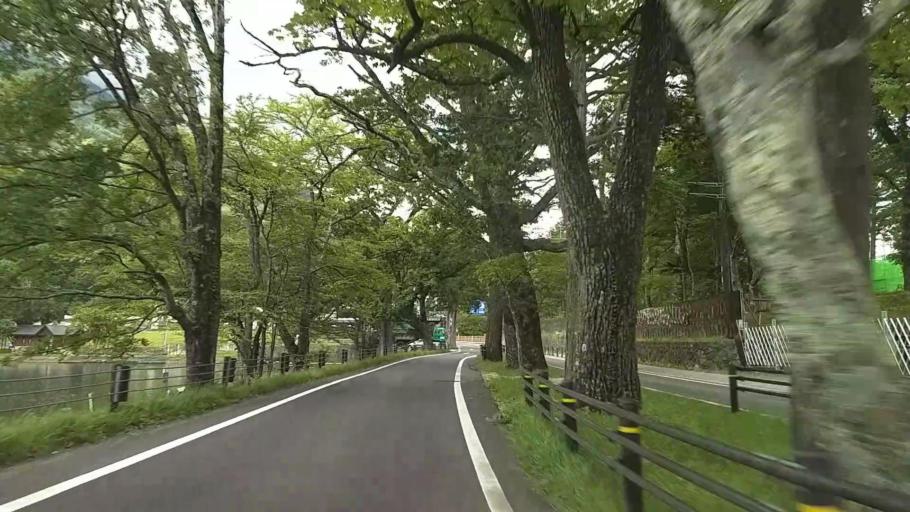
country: JP
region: Tochigi
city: Nikko
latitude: 36.7378
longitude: 139.4963
